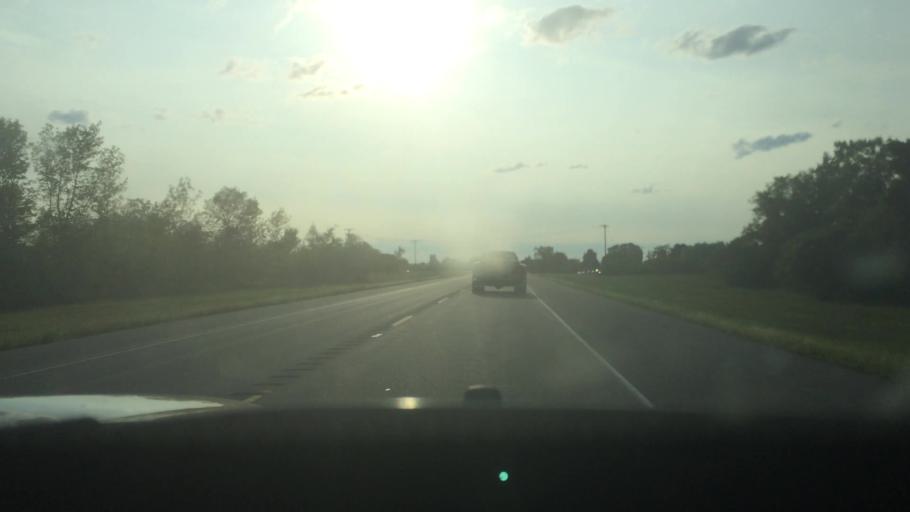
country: US
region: New York
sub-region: St. Lawrence County
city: Ogdensburg
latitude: 44.6794
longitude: -75.5115
